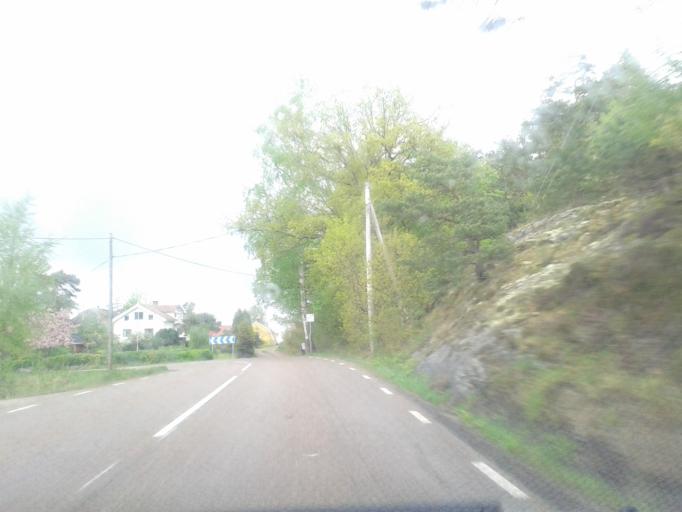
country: SE
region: Vaestra Goetaland
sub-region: Lilla Edets Kommun
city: Lilla Edet
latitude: 58.1108
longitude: 12.1161
